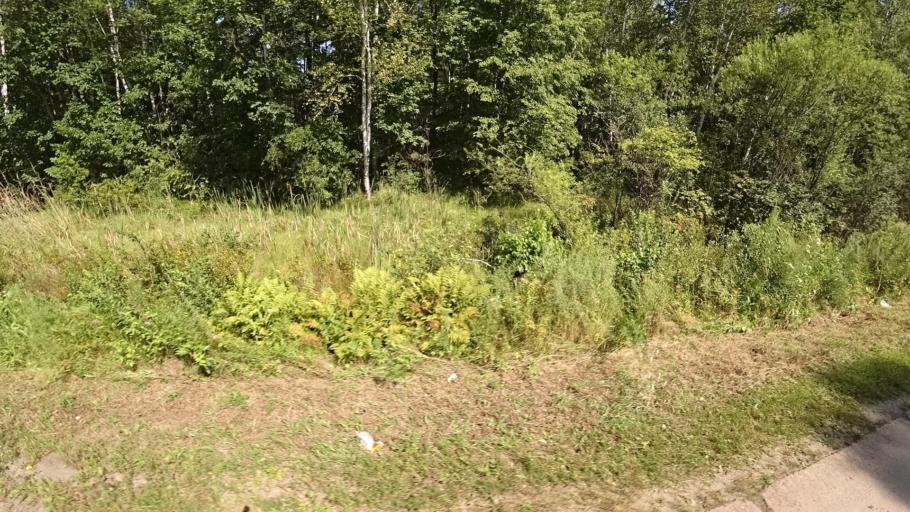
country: RU
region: Khabarovsk Krai
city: Khor
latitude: 47.9799
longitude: 135.0992
